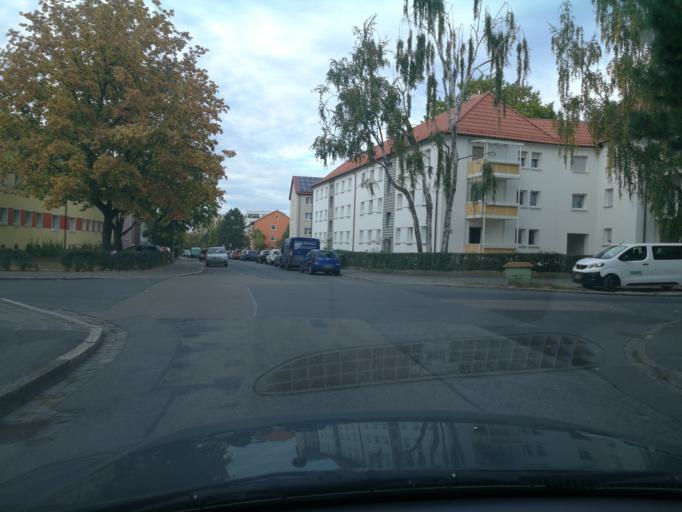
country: DE
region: Bavaria
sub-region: Regierungsbezirk Mittelfranken
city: Furth
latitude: 49.4889
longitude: 10.9716
